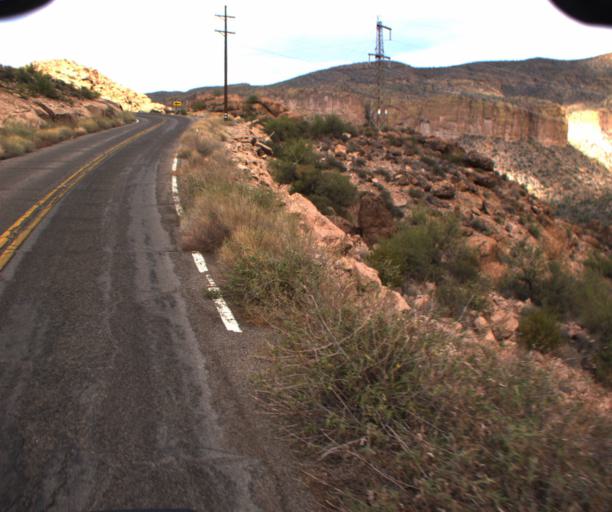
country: US
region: Arizona
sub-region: Pinal County
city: Apache Junction
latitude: 33.5280
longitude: -111.3996
